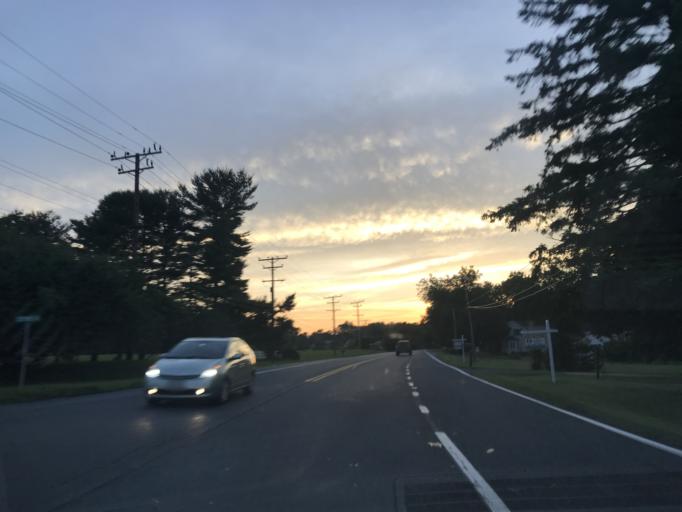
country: US
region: Maryland
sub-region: Harford County
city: Riverside
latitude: 39.5407
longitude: -76.2265
